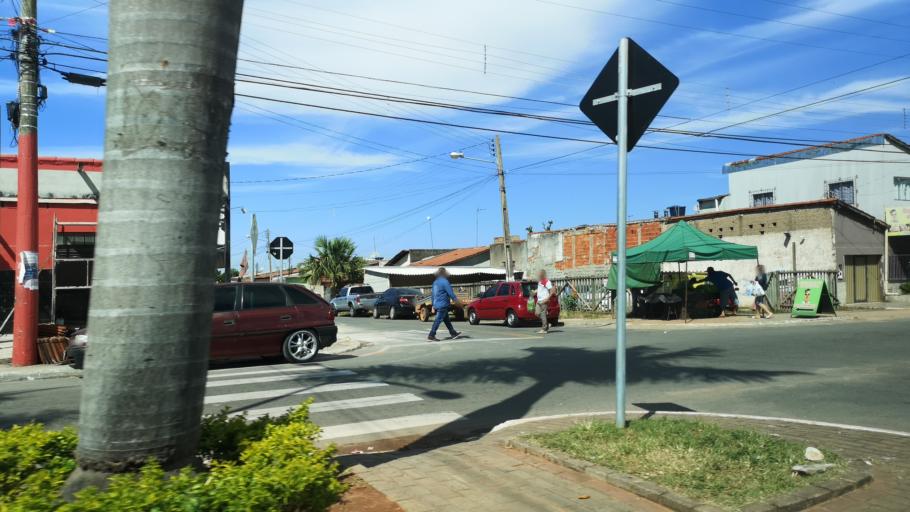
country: BR
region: Goias
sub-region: Senador Canedo
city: Senador Canedo
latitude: -16.6958
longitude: -49.1021
